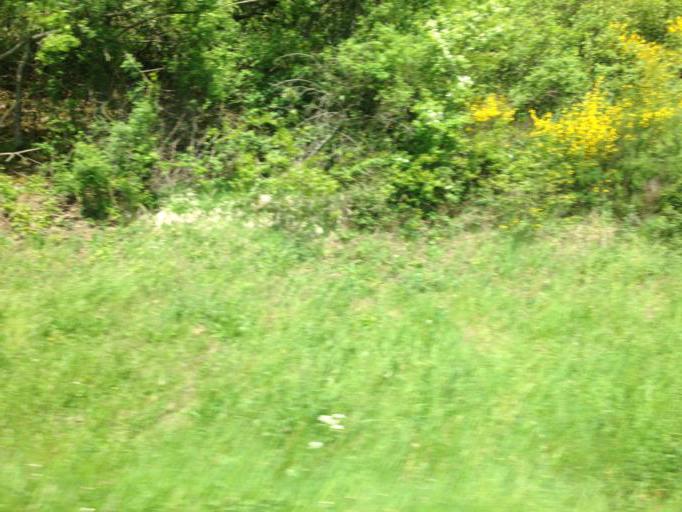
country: DE
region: North Rhine-Westphalia
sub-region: Regierungsbezirk Koln
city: Mechernich
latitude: 50.5696
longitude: 6.6982
